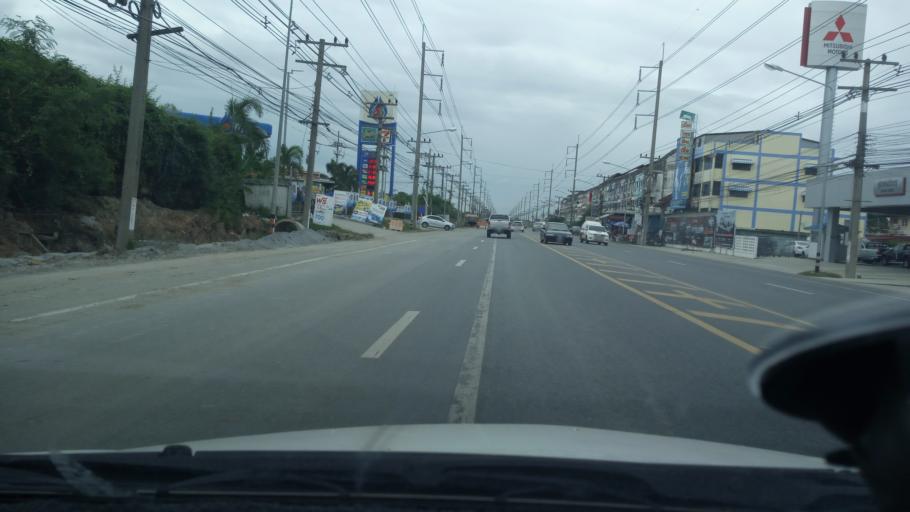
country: TH
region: Chon Buri
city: Phanat Nikhom
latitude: 13.4706
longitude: 101.1708
